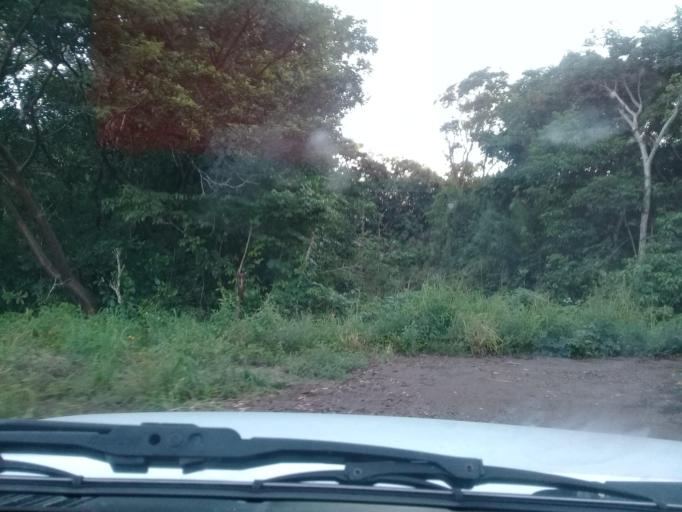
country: MX
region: Veracruz
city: Catemaco
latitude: 18.4368
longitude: -95.0816
